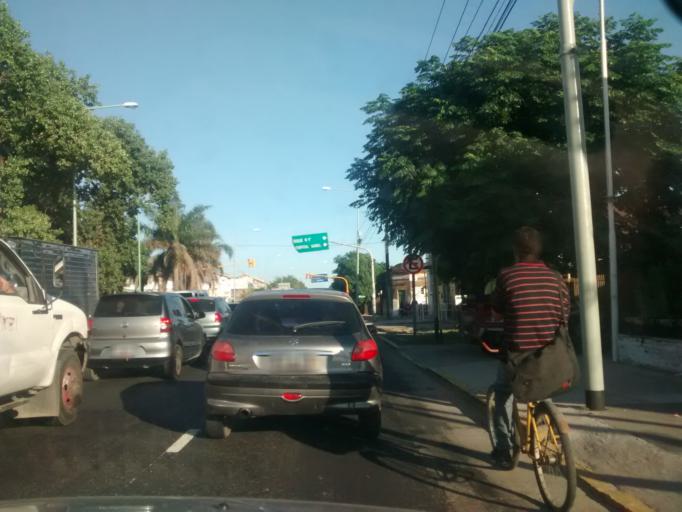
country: AR
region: Buenos Aires
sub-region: Partido de La Plata
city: La Plata
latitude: -34.9017
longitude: -57.9344
